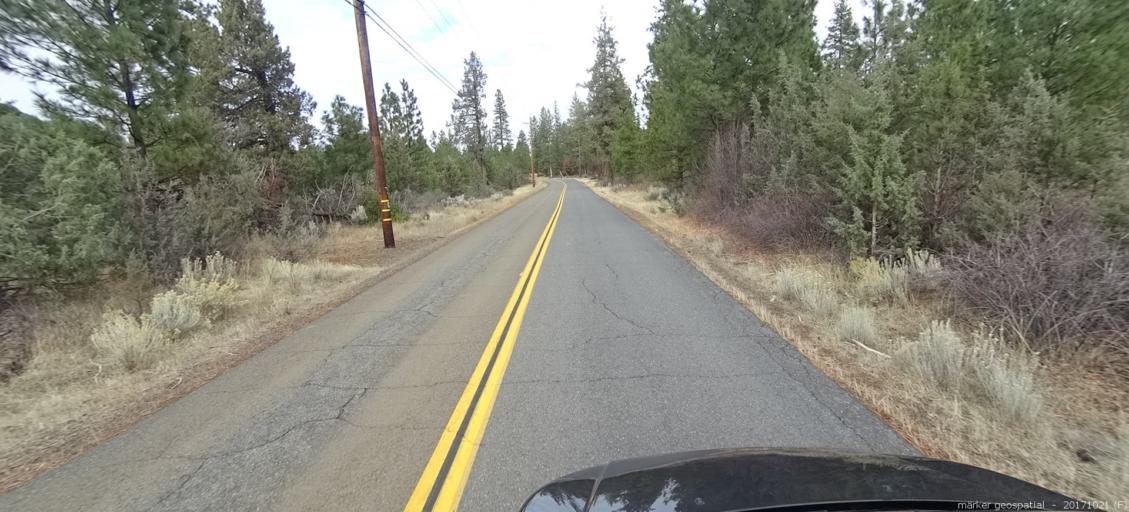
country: US
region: California
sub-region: Shasta County
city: Burney
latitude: 40.9256
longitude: -121.6457
